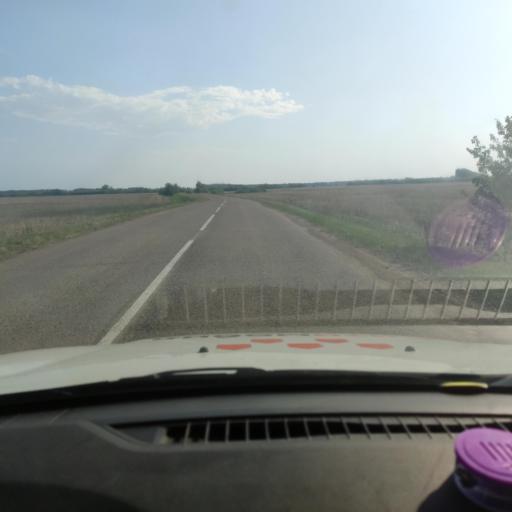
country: RU
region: Bashkortostan
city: Asanovo
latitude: 54.9929
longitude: 55.5686
